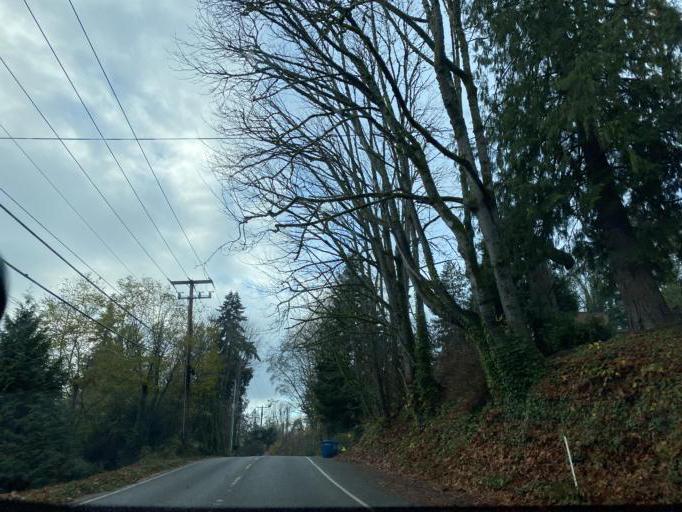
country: US
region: Washington
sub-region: King County
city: Mercer Island
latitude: 47.5365
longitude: -122.2132
